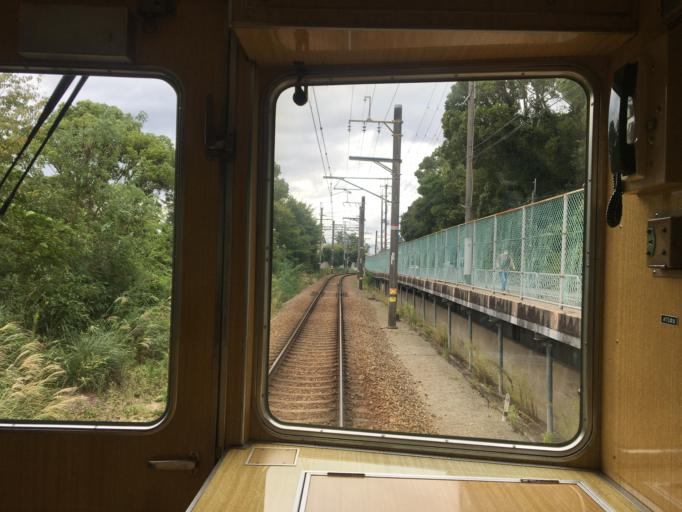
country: JP
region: Hyogo
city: Ashiya
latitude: 34.7587
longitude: 135.3321
